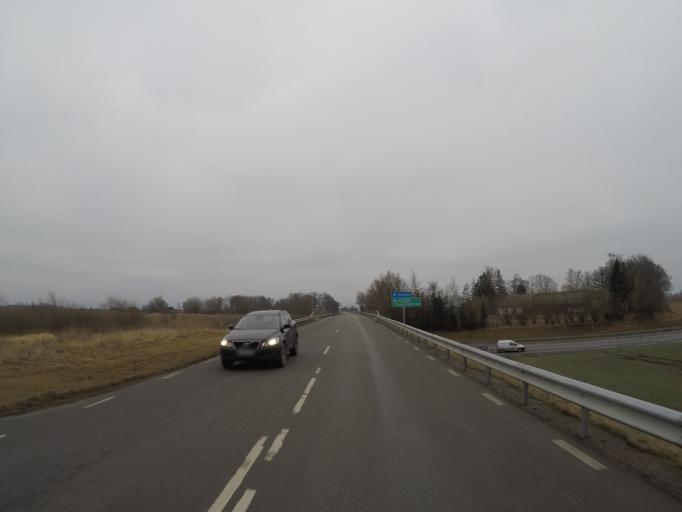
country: SE
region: Skane
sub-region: Hoors Kommun
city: Loberod
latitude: 55.7854
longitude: 13.4155
